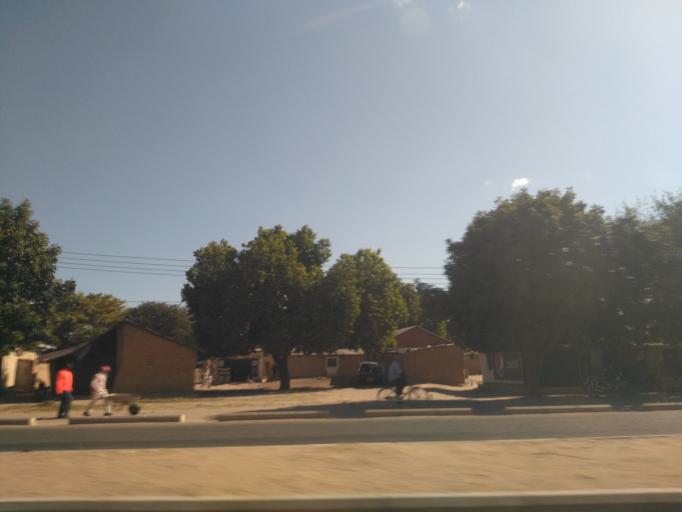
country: TZ
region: Dodoma
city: Dodoma
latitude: -6.1677
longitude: 35.7243
